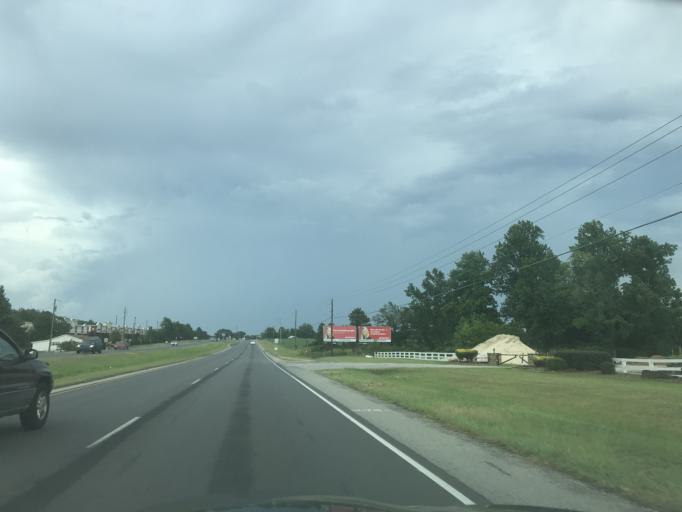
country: US
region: North Carolina
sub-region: Johnston County
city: Clayton
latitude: 35.6297
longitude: -78.4322
